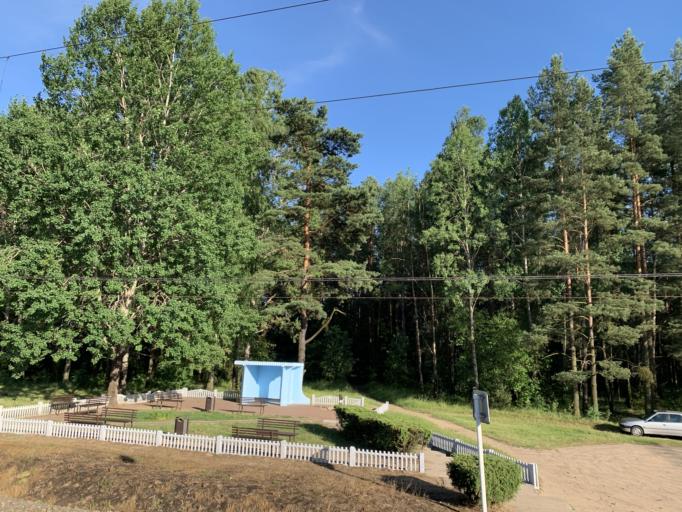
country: BY
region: Minsk
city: Enyerhyetykaw
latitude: 53.5285
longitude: 26.9258
